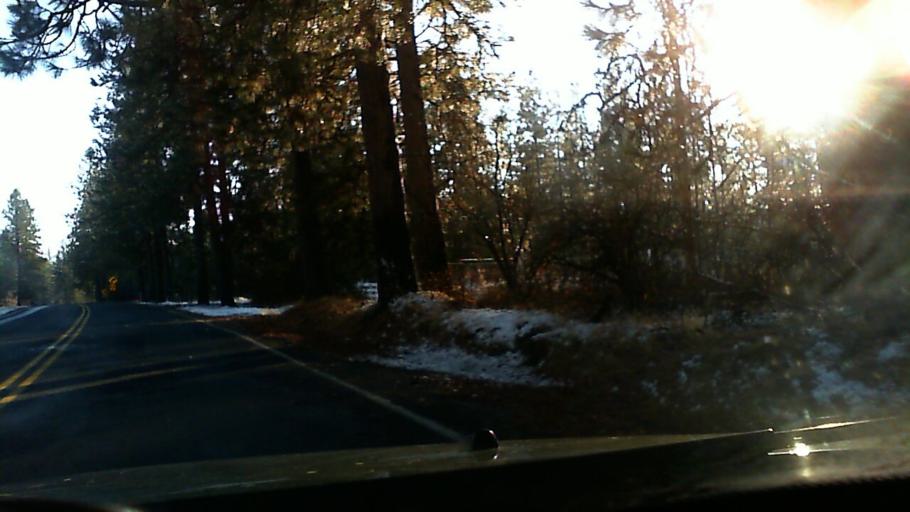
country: US
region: Washington
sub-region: Spokane County
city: Trentwood
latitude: 47.7256
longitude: -117.2130
